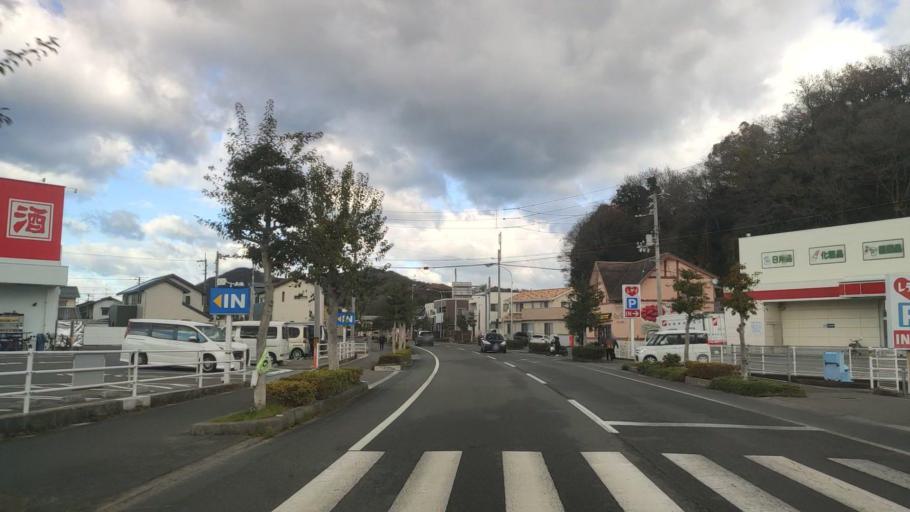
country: JP
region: Ehime
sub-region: Shikoku-chuo Shi
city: Matsuyama
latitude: 33.8680
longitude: 132.7243
